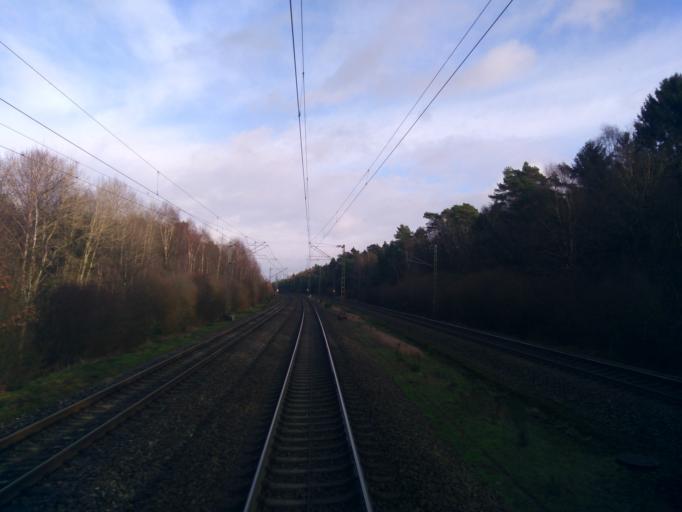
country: DE
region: Lower Saxony
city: Lauenbruck
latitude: 53.2013
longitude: 9.5787
